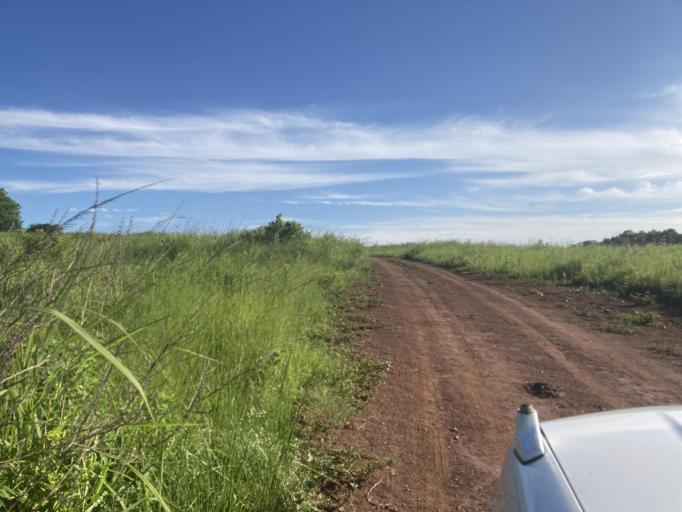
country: SZ
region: Hhohho
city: Lobamba
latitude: -26.4917
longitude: 31.1925
